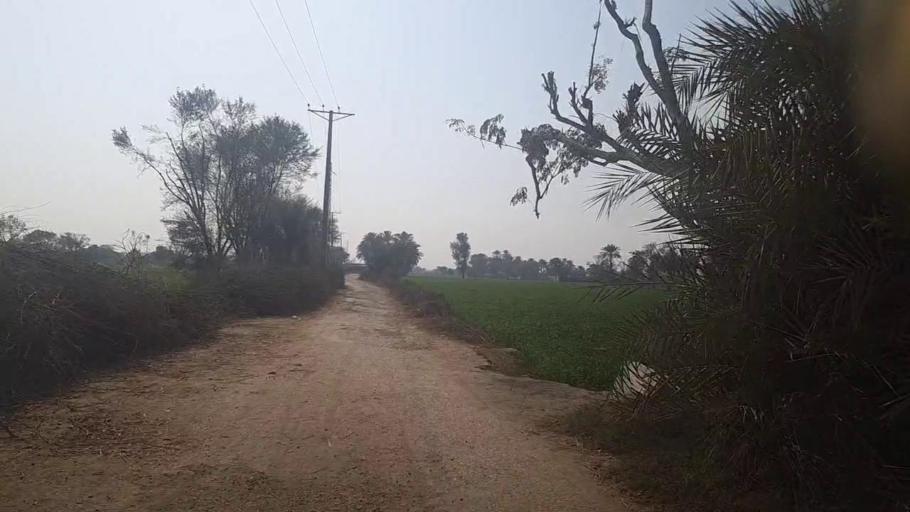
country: PK
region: Sindh
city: Kot Diji
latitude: 27.3509
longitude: 68.7337
